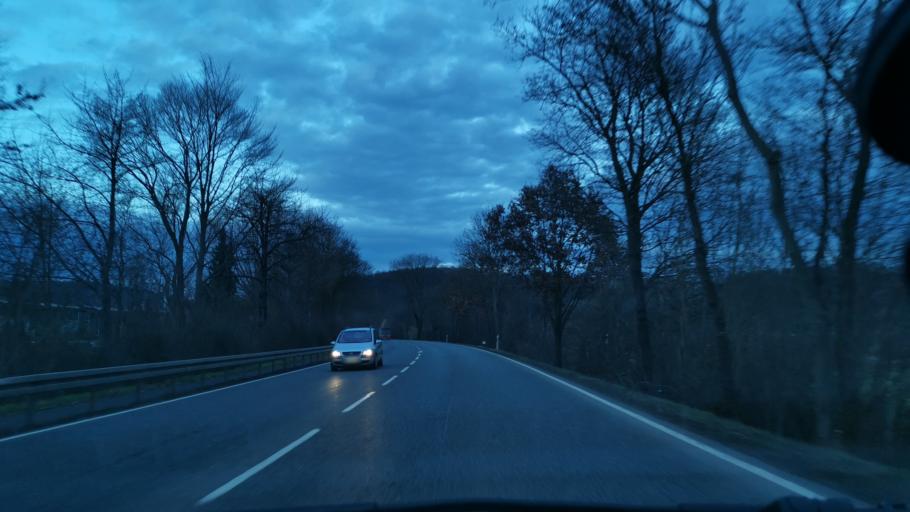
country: DE
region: Hesse
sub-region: Regierungsbezirk Kassel
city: Bad Hersfeld
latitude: 50.8676
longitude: 9.7229
